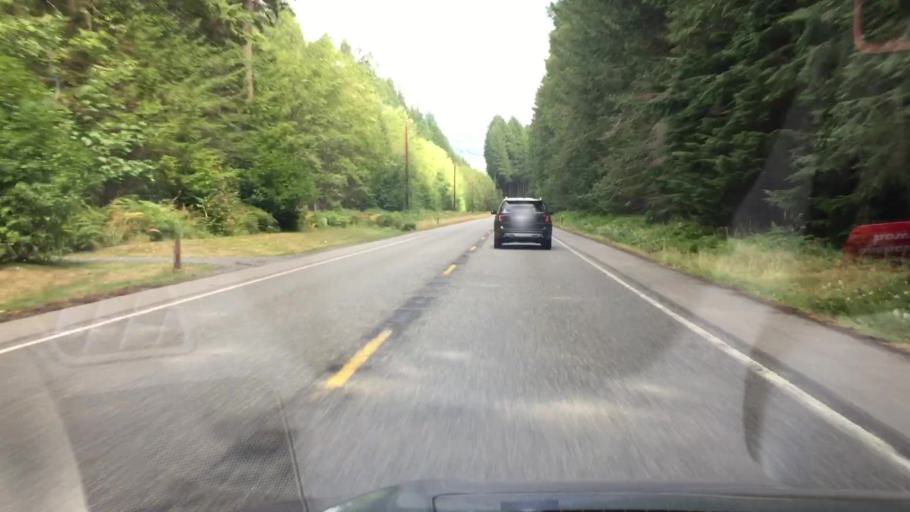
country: US
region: Washington
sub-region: Pierce County
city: Eatonville
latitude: 46.7551
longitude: -122.0991
